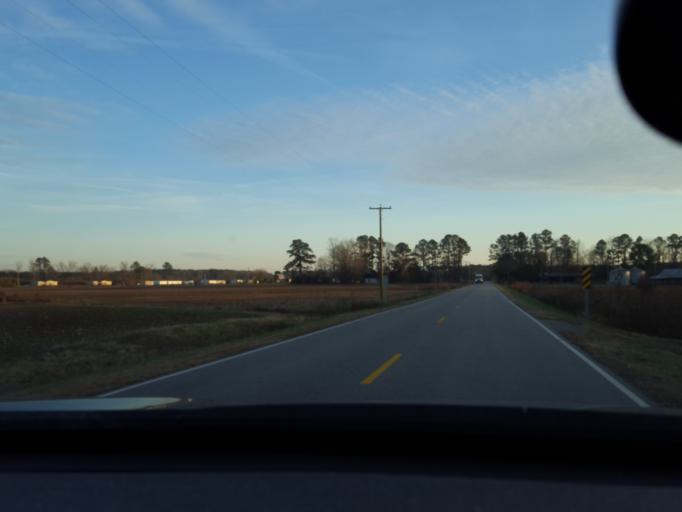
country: US
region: North Carolina
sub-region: Hertford County
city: Ahoskie
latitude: 36.2479
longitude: -77.1203
